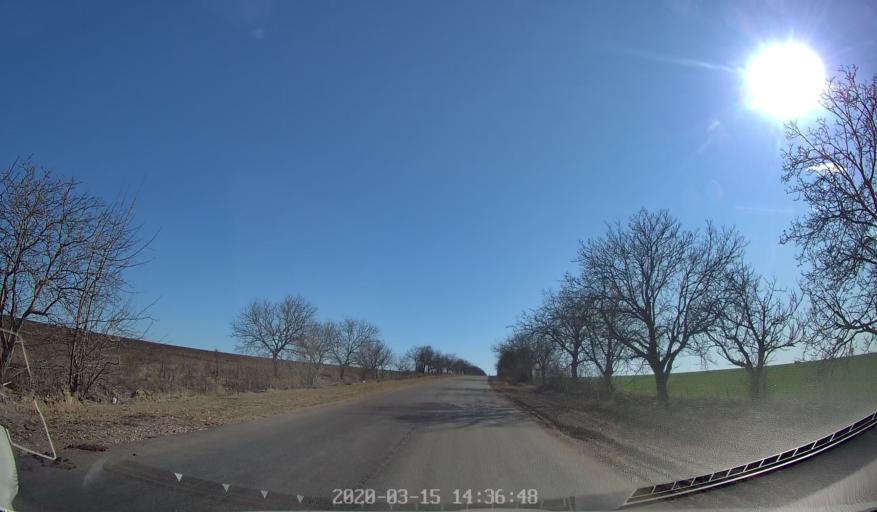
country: MD
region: Orhei
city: Orhei
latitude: 47.3230
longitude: 28.9256
